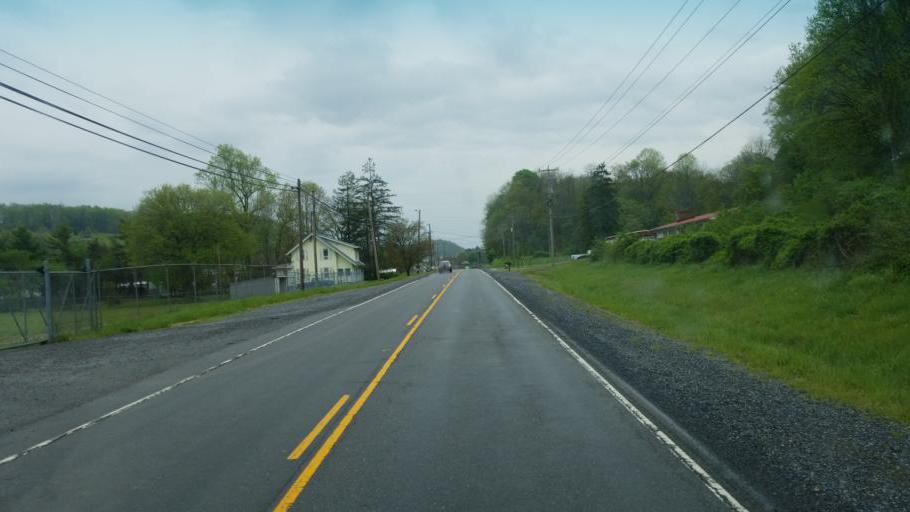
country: US
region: Virginia
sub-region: Smyth County
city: Atkins
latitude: 36.8564
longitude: -81.4671
